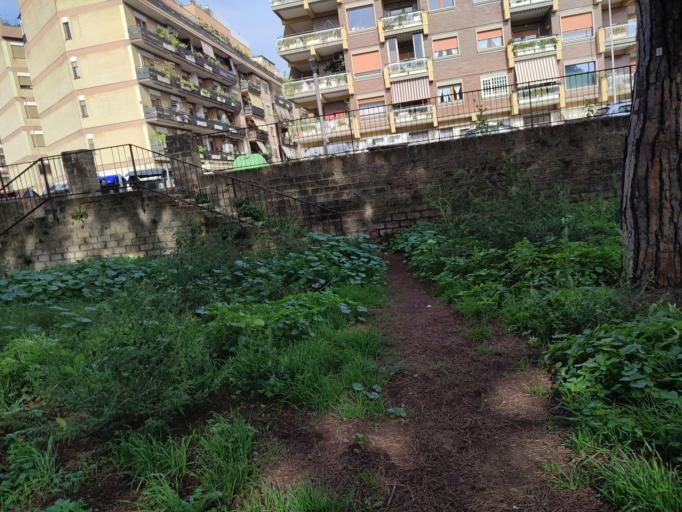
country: IT
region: Latium
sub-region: Citta metropolitana di Roma Capitale
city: Lido di Ostia
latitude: 41.7330
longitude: 12.2998
